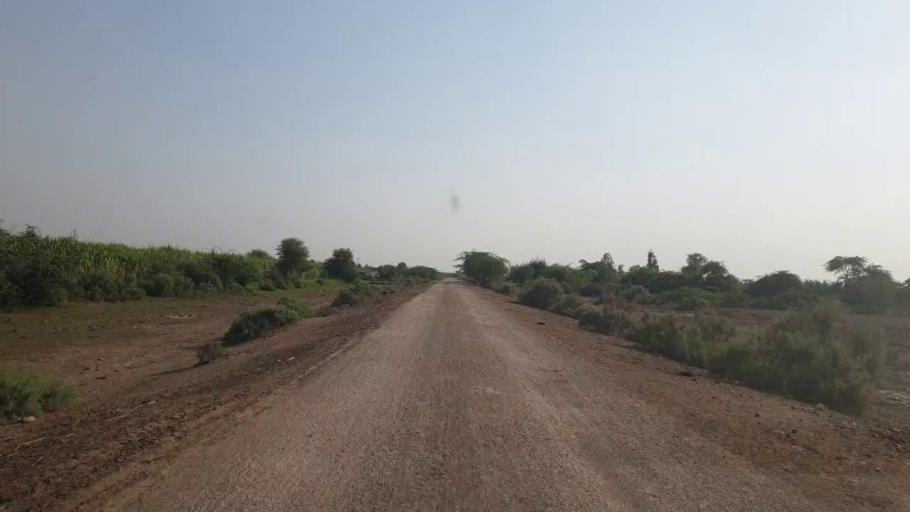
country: PK
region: Sindh
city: Sanghar
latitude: 26.0446
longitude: 68.8975
